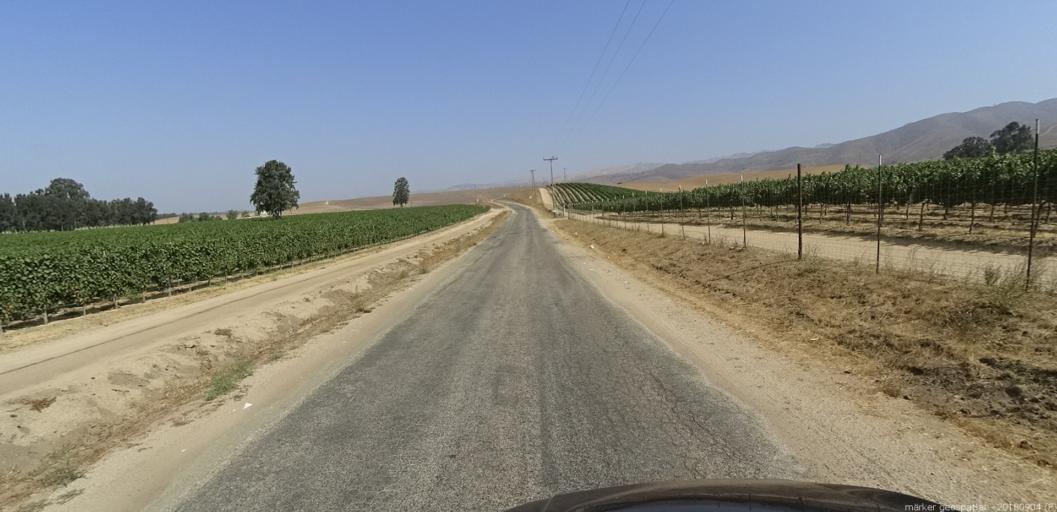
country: US
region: California
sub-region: Monterey County
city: Soledad
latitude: 36.4788
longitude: -121.3498
